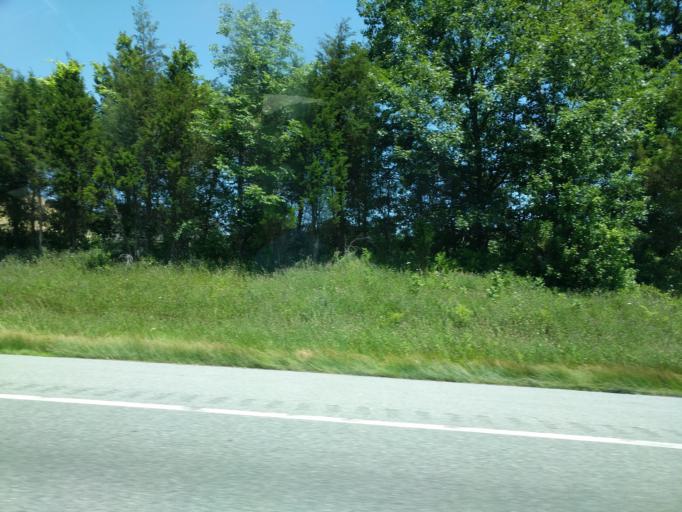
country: US
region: New York
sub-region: Orange County
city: Kiryas Joel
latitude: 41.3253
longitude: -74.1563
